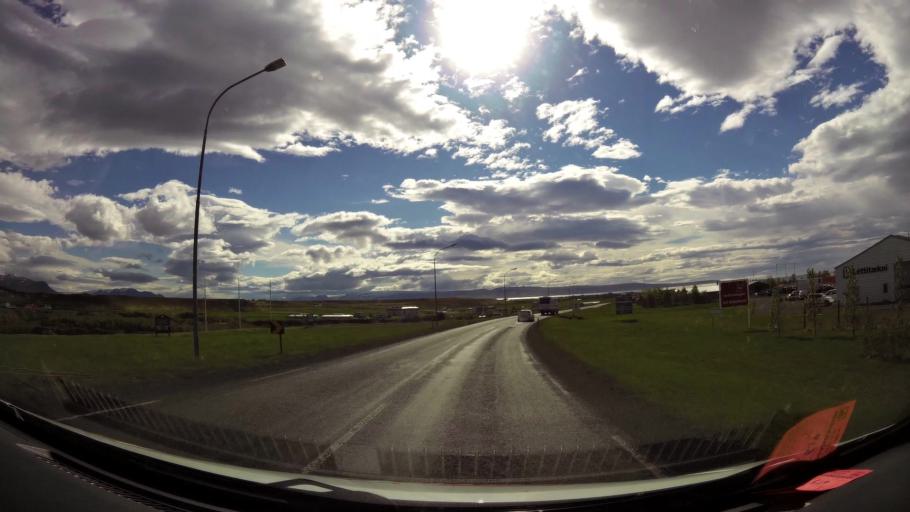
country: IS
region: Northwest
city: Saudarkrokur
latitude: 65.6603
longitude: -20.2677
